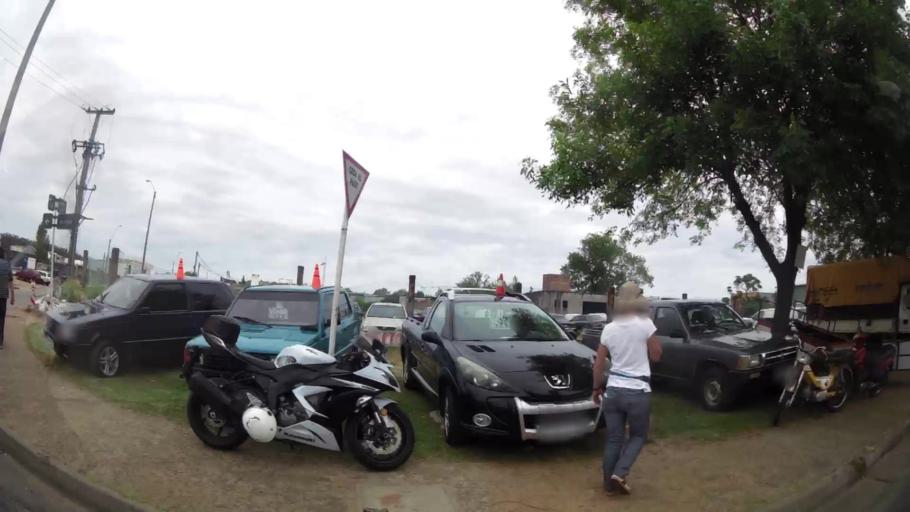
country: UY
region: Maldonado
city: Maldonado
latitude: -34.9081
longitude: -54.9436
